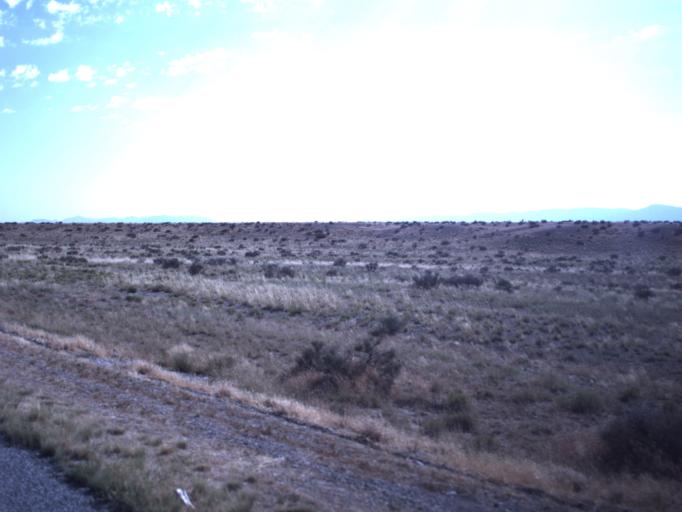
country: US
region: Utah
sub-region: Millard County
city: Fillmore
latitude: 38.9046
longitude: -112.8199
